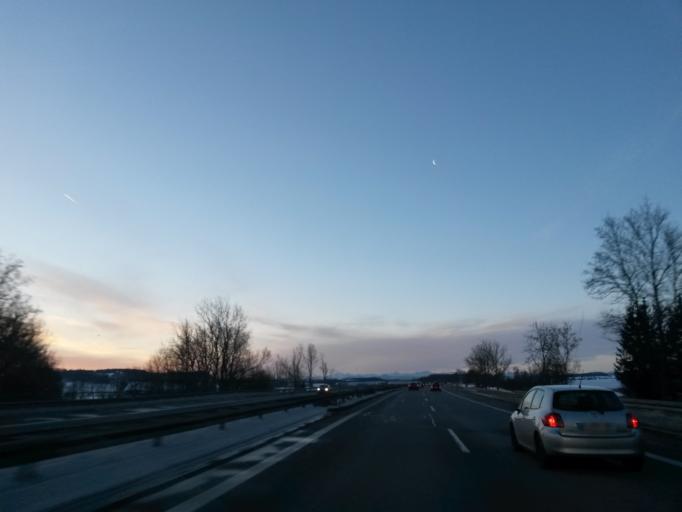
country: DE
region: Bavaria
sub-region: Swabia
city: Wolfertschwenden
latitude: 47.8994
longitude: 10.2439
